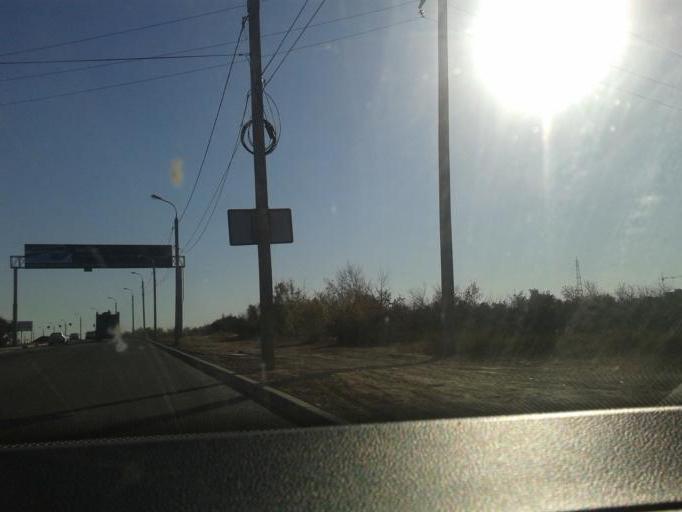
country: RU
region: Volgograd
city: Volgograd
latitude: 48.7488
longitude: 44.5258
